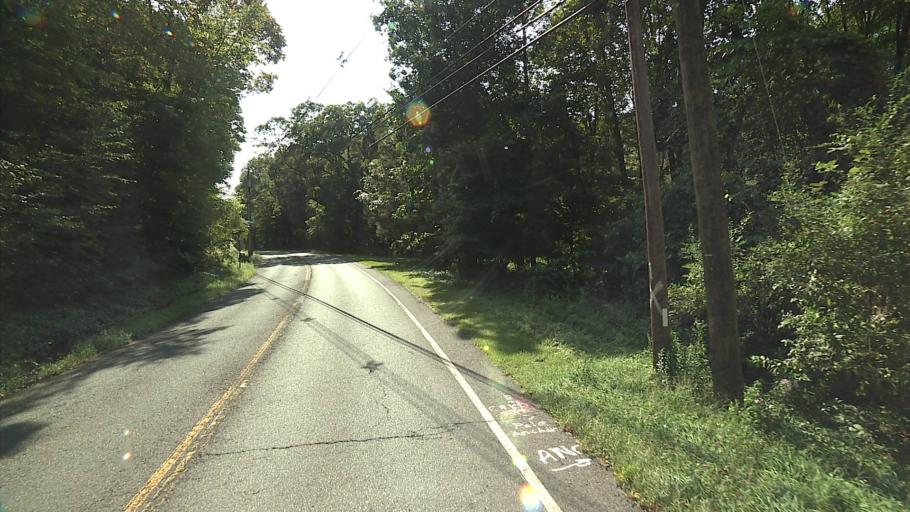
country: US
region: Connecticut
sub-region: New Haven County
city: Heritage Village
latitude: 41.5052
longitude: -73.2524
